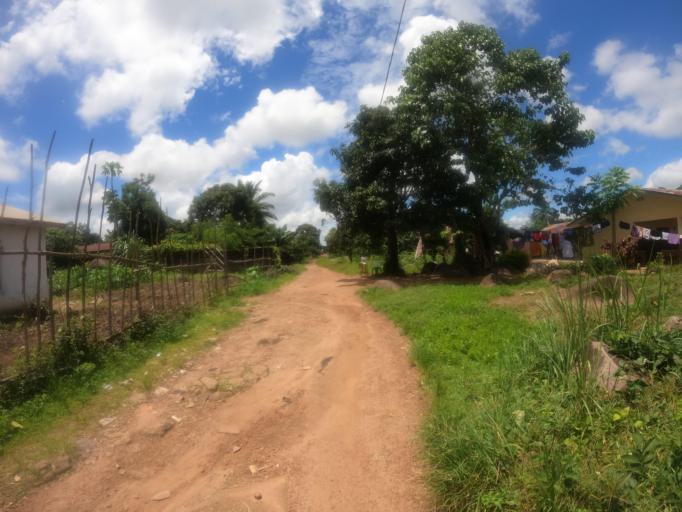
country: SL
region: Northern Province
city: Makeni
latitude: 8.8883
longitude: -12.0695
